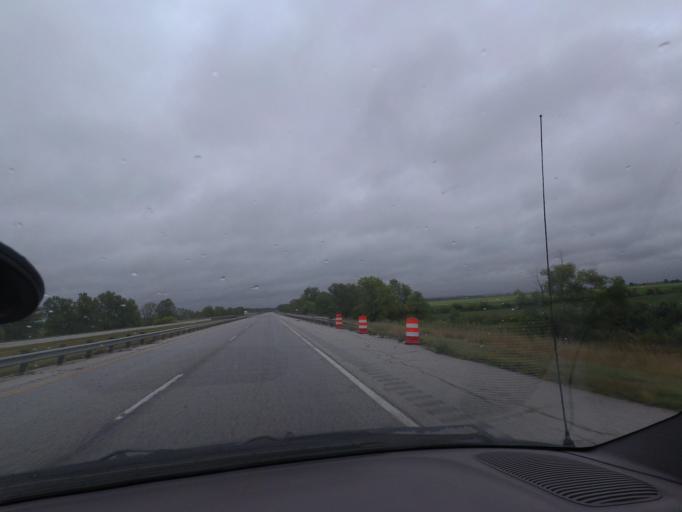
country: US
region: Illinois
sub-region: Pike County
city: Griggsville
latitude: 39.6918
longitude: -90.6214
